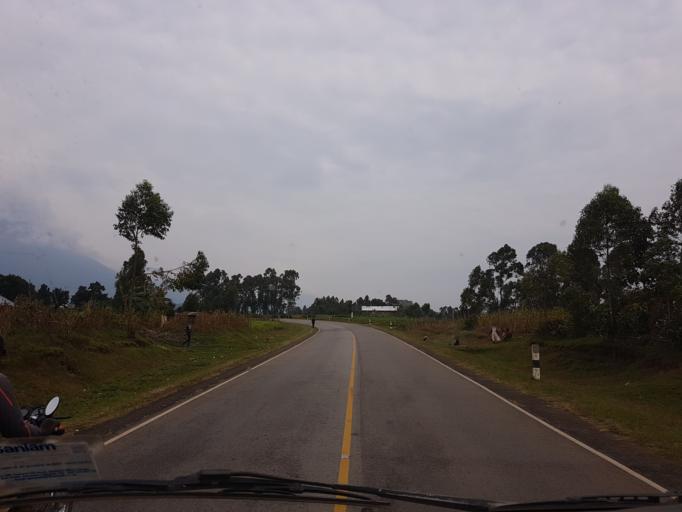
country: UG
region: Western Region
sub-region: Kisoro District
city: Kisoro
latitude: -1.3078
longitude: 29.7227
